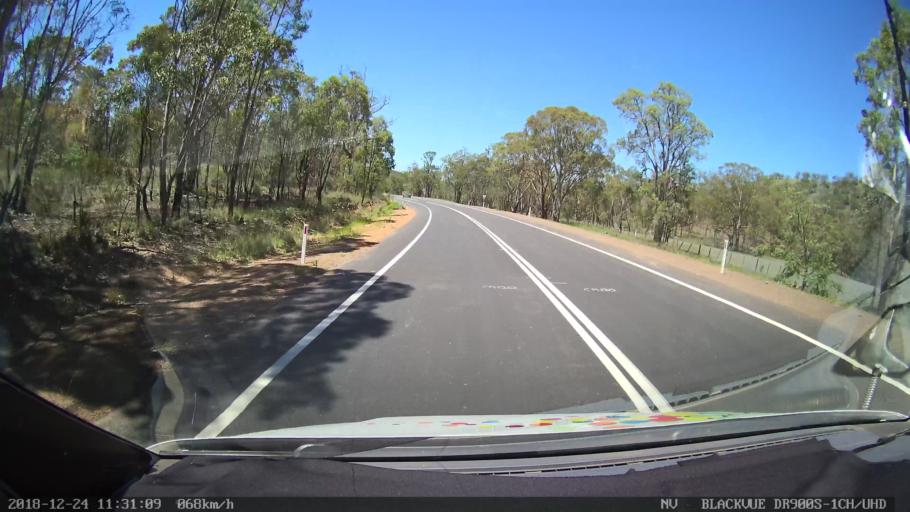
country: AU
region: New South Wales
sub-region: Upper Hunter Shire
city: Merriwa
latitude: -32.2120
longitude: 150.4612
